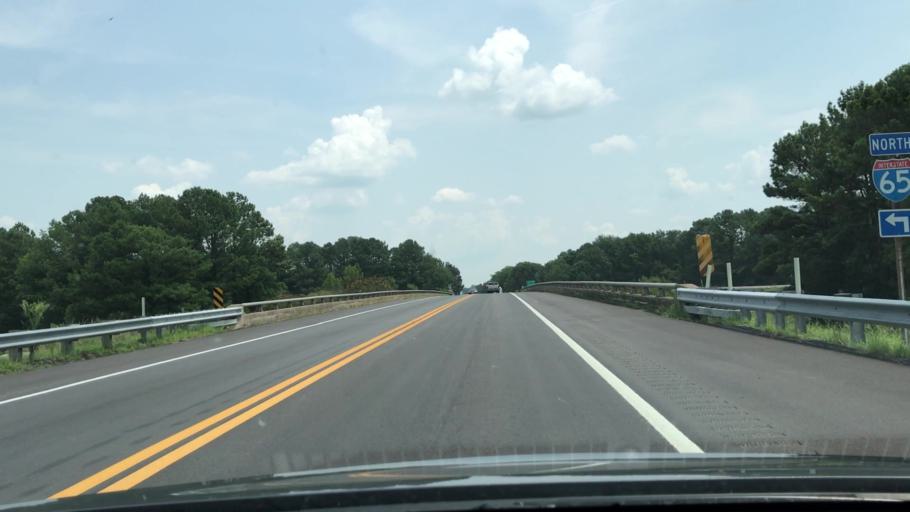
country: US
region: Tennessee
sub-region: Sumner County
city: Portland
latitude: 36.5914
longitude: -86.6014
